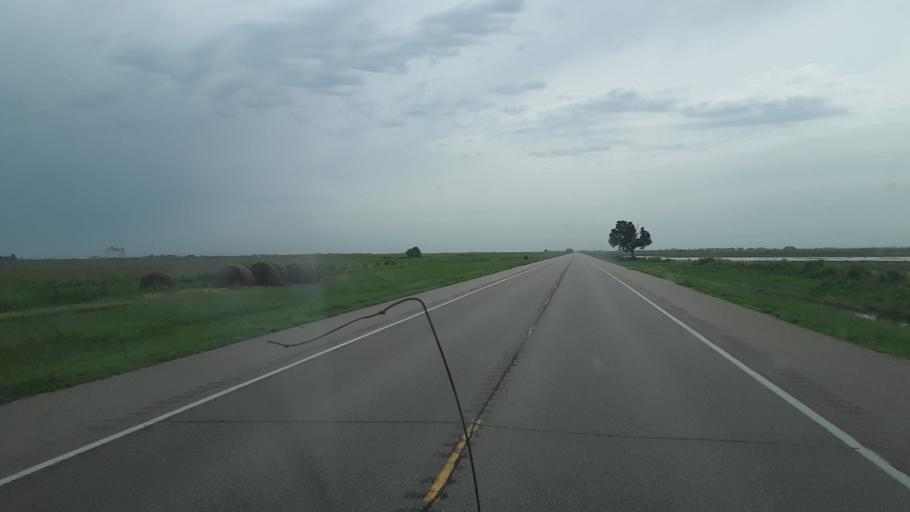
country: US
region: Kansas
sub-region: Stafford County
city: Saint John
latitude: 37.9563
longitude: -98.9103
